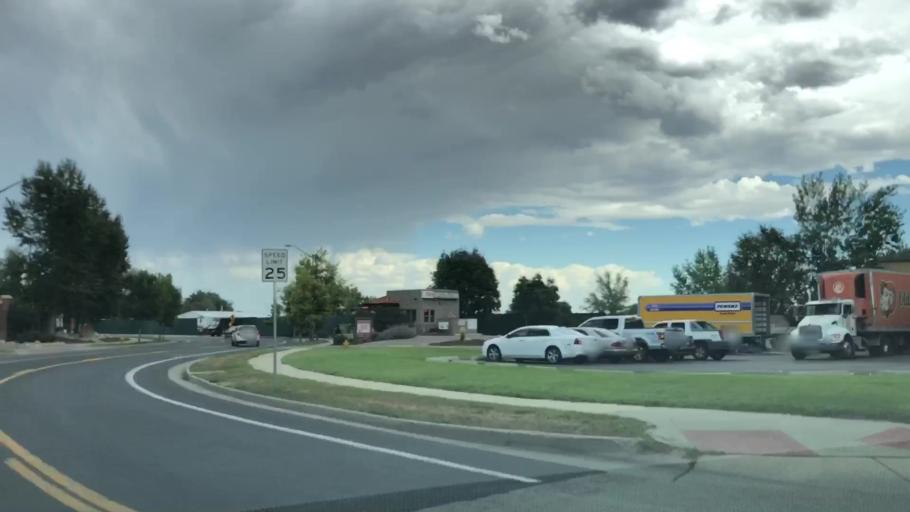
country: US
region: Colorado
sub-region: Larimer County
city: Fort Collins
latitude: 40.5822
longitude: -105.0543
